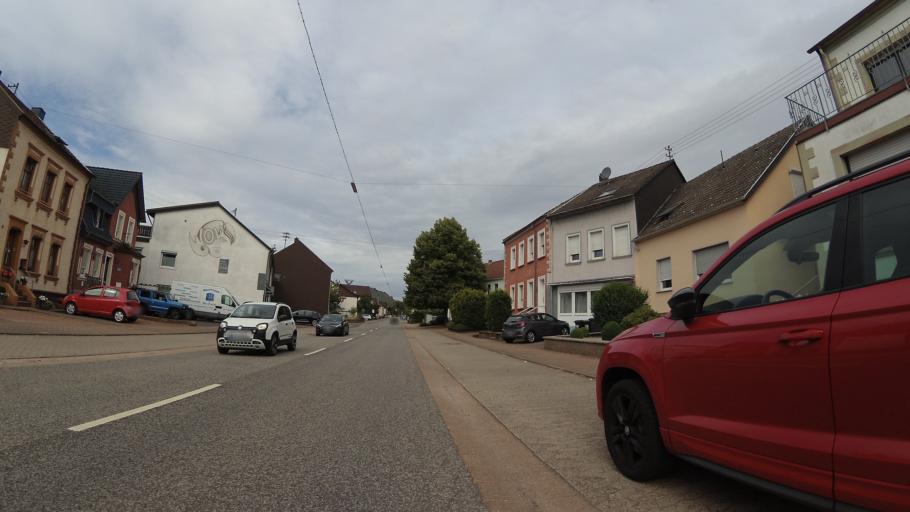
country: DE
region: Saarland
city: Schwalbach
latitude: 49.3191
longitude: 6.8075
